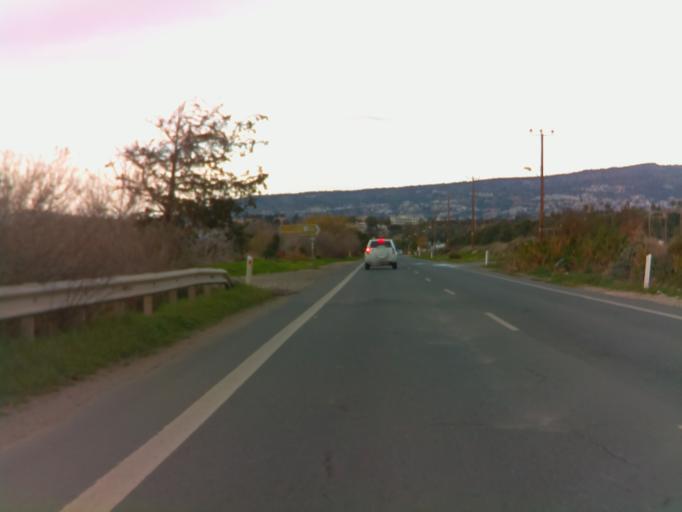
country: CY
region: Pafos
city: Kissonerga
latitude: 34.8437
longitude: 32.3874
